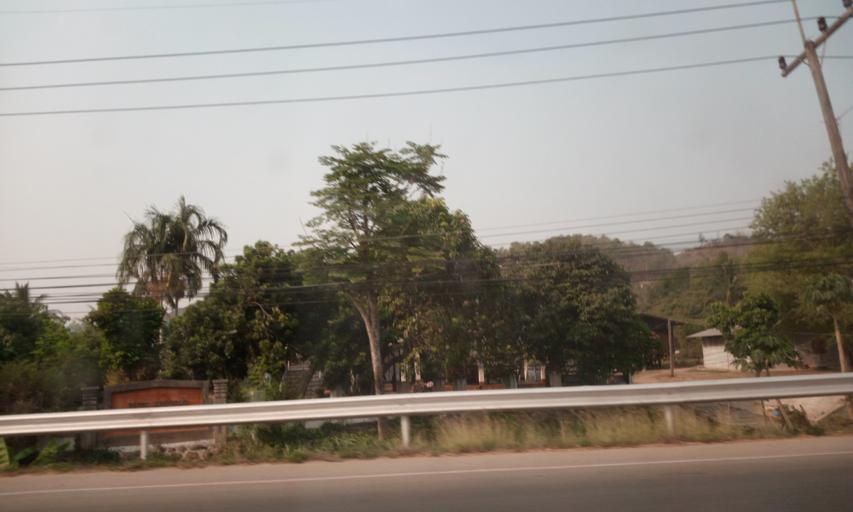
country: TH
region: Chiang Rai
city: Pa Daet
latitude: 19.6167
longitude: 99.9967
